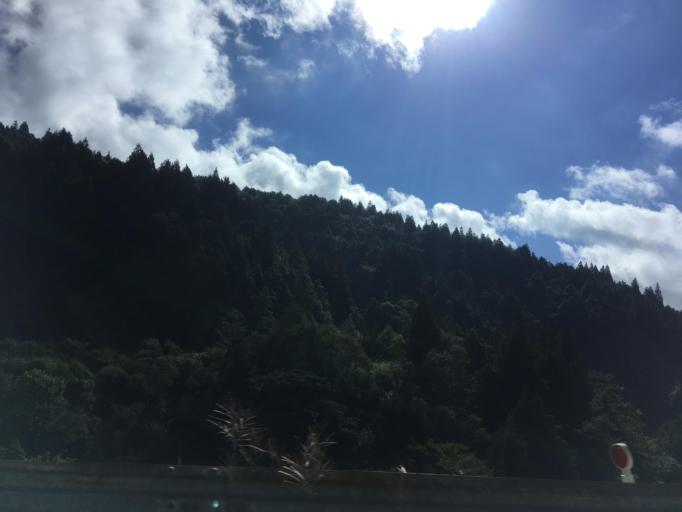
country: TW
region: Taiwan
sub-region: Yilan
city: Yilan
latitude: 24.5185
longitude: 121.5726
